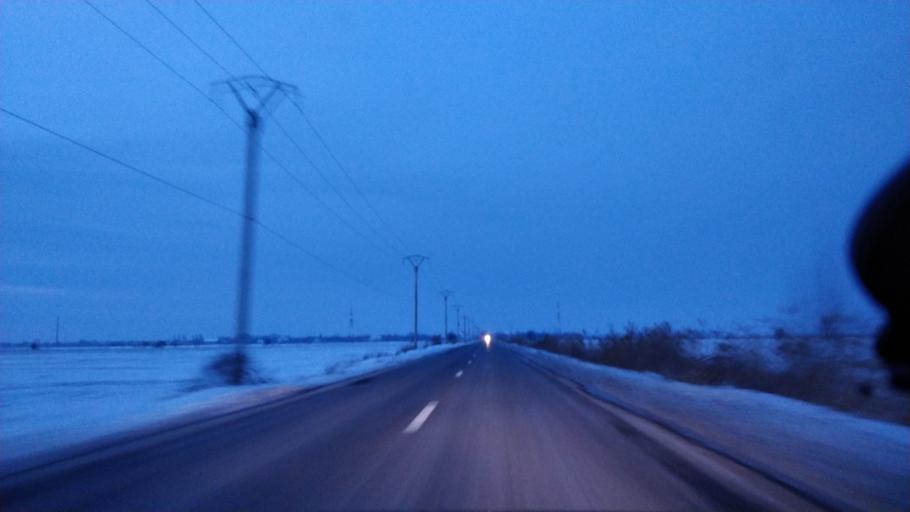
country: RO
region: Vrancea
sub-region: Comuna Nanesti
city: Nanesti
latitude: 45.5782
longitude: 27.4975
